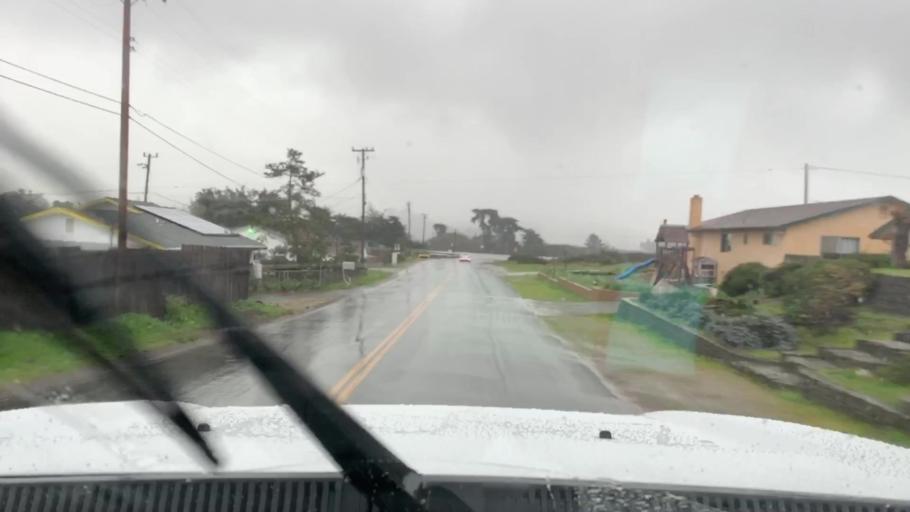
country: US
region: California
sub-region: San Luis Obispo County
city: Los Osos
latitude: 35.3220
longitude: -120.8234
